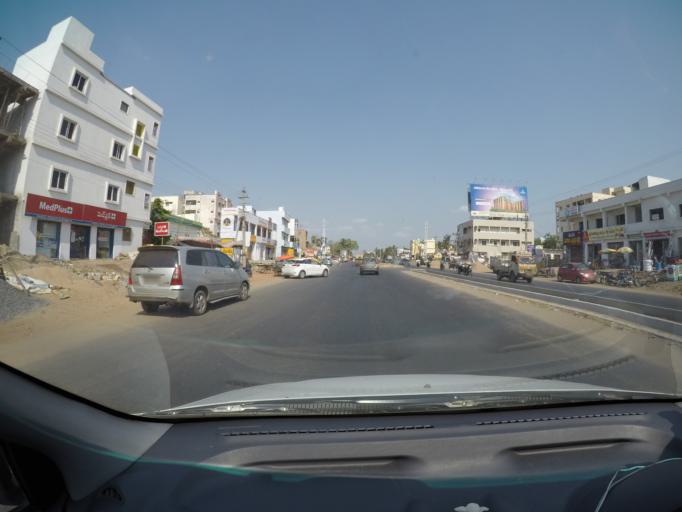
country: IN
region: Andhra Pradesh
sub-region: Krishna
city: Yanamalakuduru
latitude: 16.4766
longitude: 80.7060
